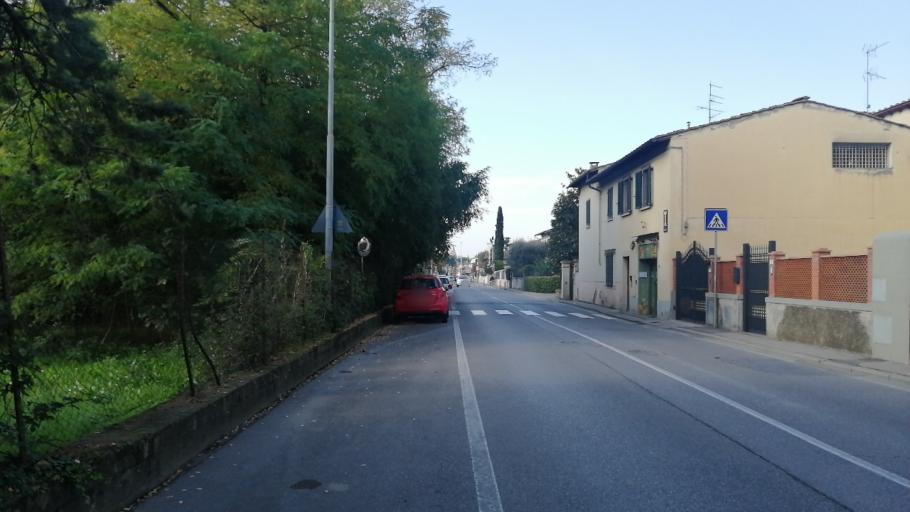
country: IT
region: Tuscany
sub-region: Province of Florence
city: Bagno a Ripoli
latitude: 43.7535
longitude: 11.3090
